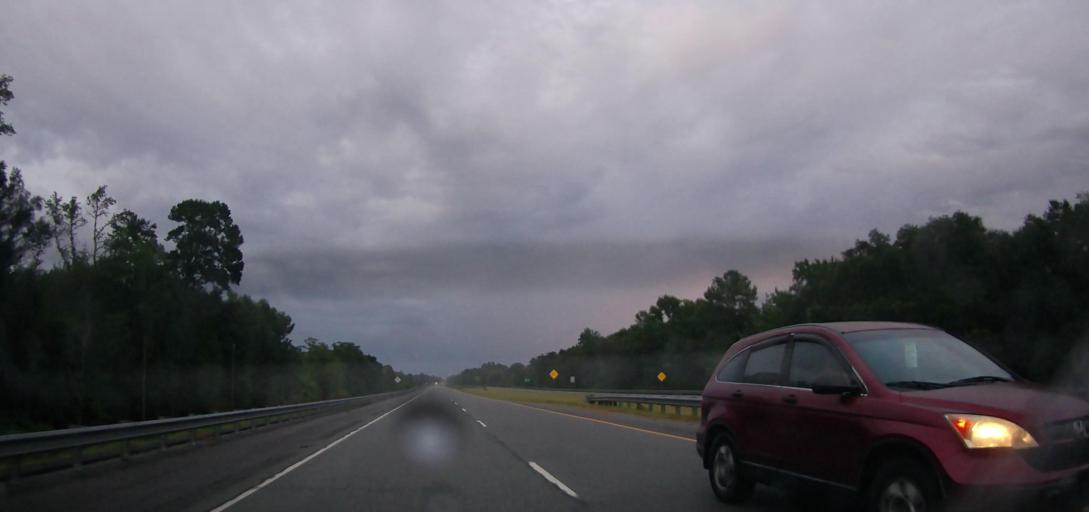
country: US
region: Georgia
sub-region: Lanier County
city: Lakeland
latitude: 30.9249
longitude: -83.0363
